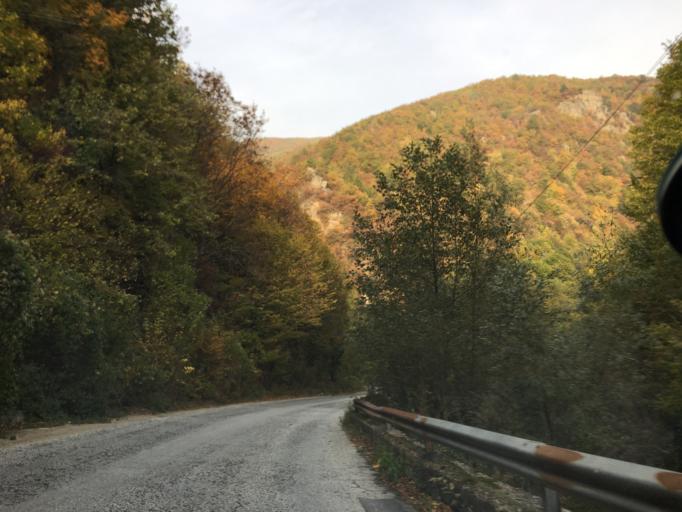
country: BG
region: Pazardzhik
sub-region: Obshtina Belovo
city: Belovo
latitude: 42.1467
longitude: 23.9686
